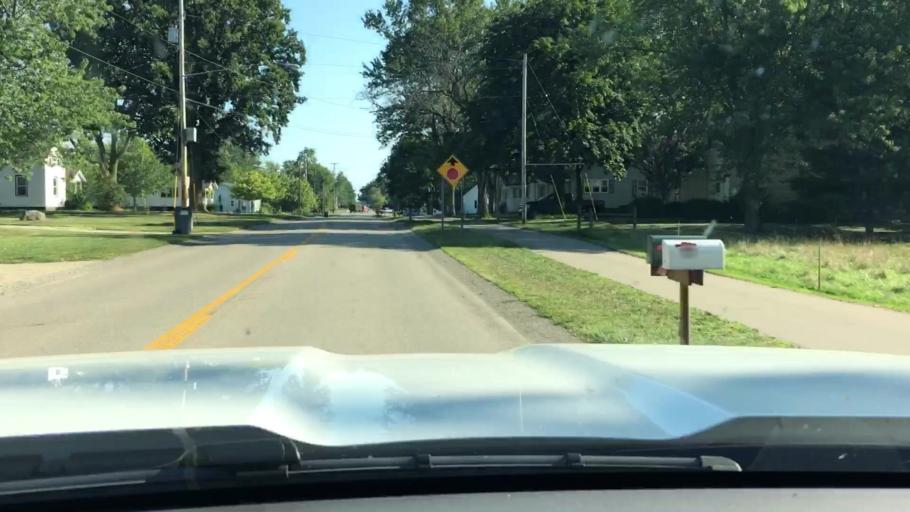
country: US
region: Michigan
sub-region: Ottawa County
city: Zeeland
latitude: 42.7852
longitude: -85.9404
